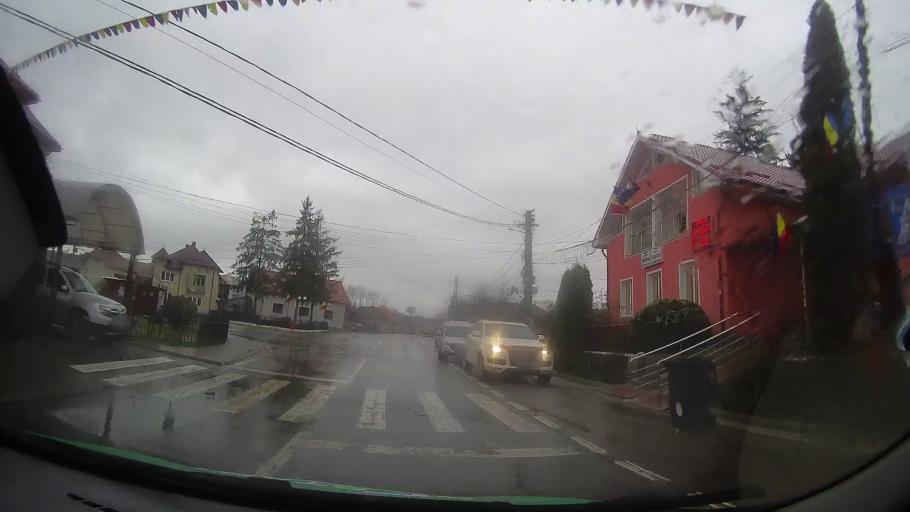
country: RO
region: Bistrita-Nasaud
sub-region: Comuna Monor
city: Monor
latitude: 46.9502
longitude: 24.6927
